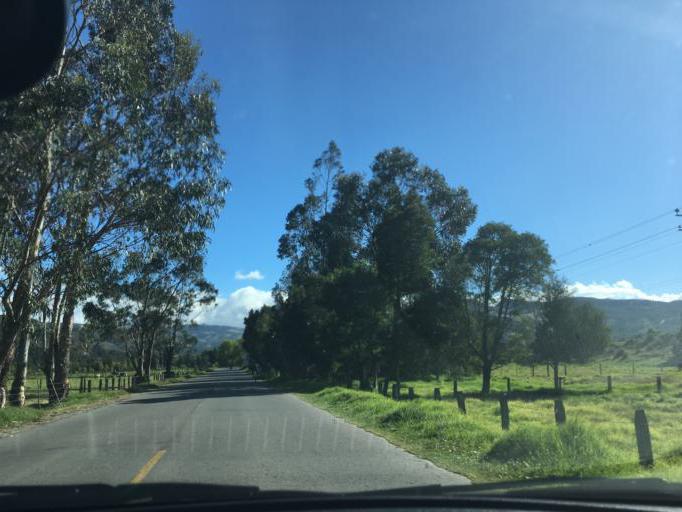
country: CO
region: Boyaca
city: Firavitoba
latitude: 5.6357
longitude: -72.9862
